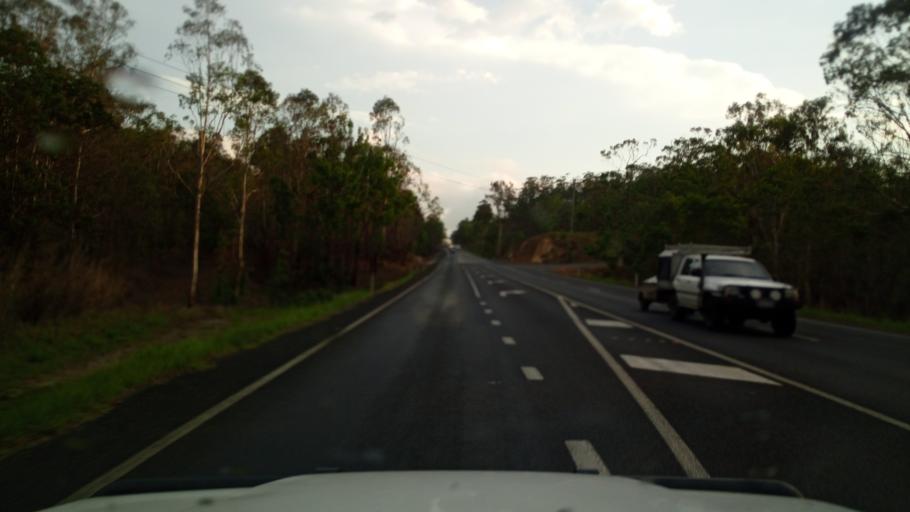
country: AU
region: Queensland
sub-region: Tablelands
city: Kuranda
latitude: -16.8538
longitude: 145.6011
